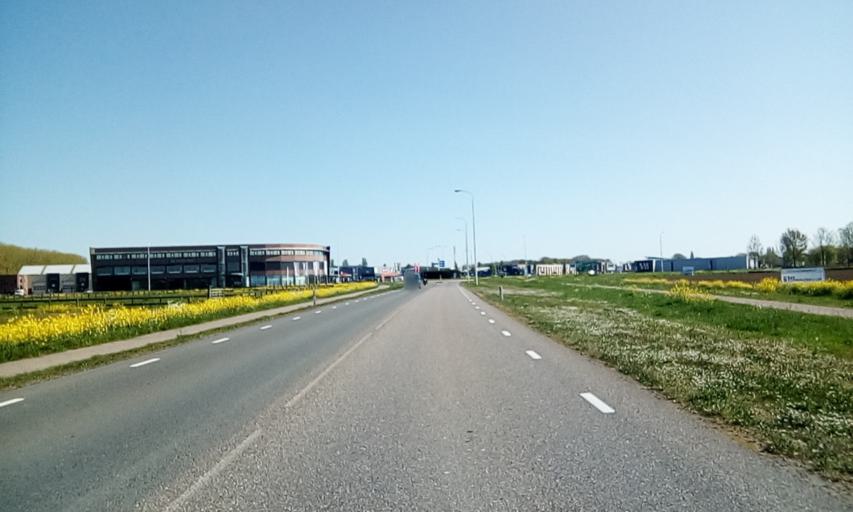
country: NL
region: Gelderland
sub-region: Gemeente Druten
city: Druten
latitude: 51.8821
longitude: 5.5711
